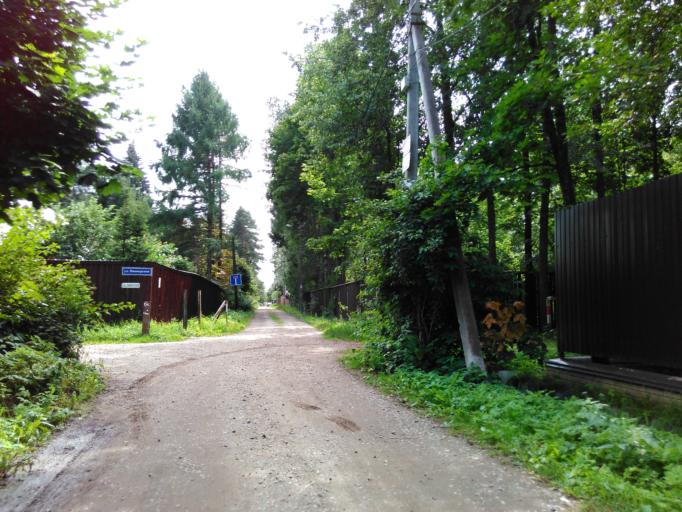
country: RU
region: Moskovskaya
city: Pravdinskiy
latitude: 56.0582
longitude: 37.8392
